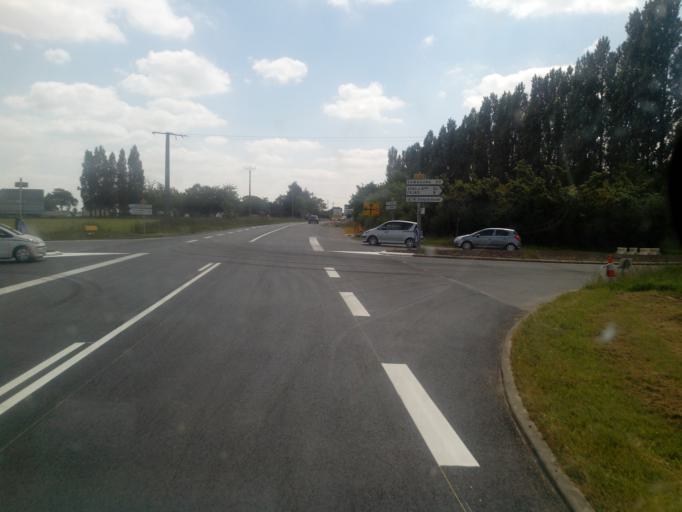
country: FR
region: Brittany
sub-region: Departement d'Ille-et-Vilaine
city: Sens-de-Bretagne
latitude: 48.3335
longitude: -1.5235
